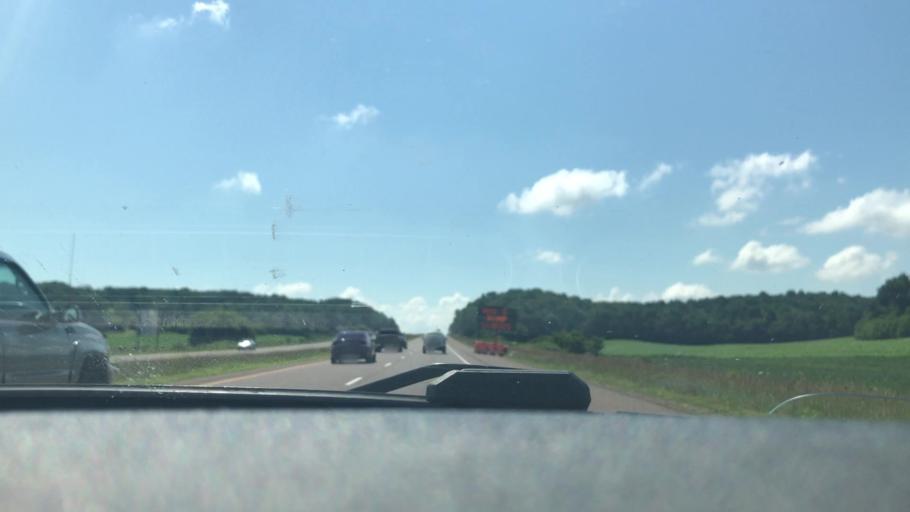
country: US
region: Wisconsin
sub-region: Chippewa County
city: Chippewa Falls
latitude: 44.9822
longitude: -91.4402
